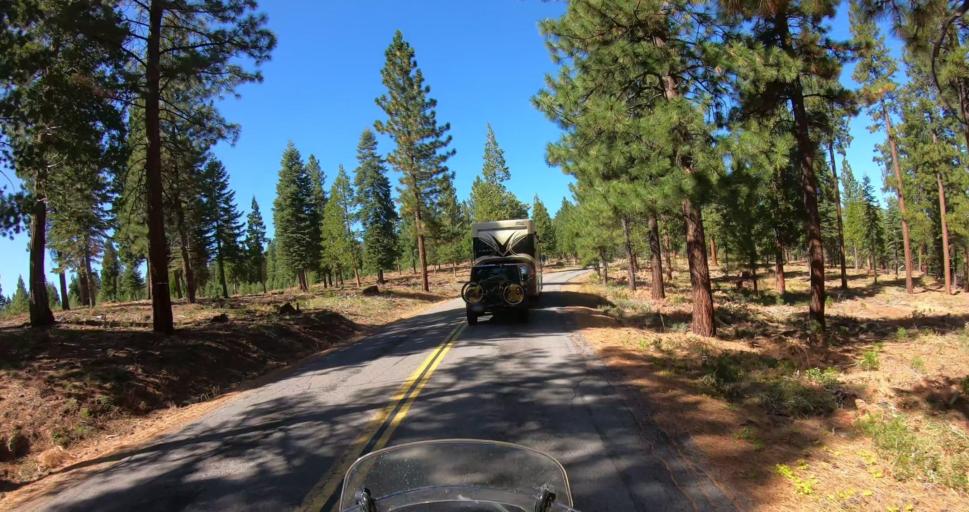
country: US
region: California
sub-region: Lassen County
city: Susanville
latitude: 40.4457
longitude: -120.7578
